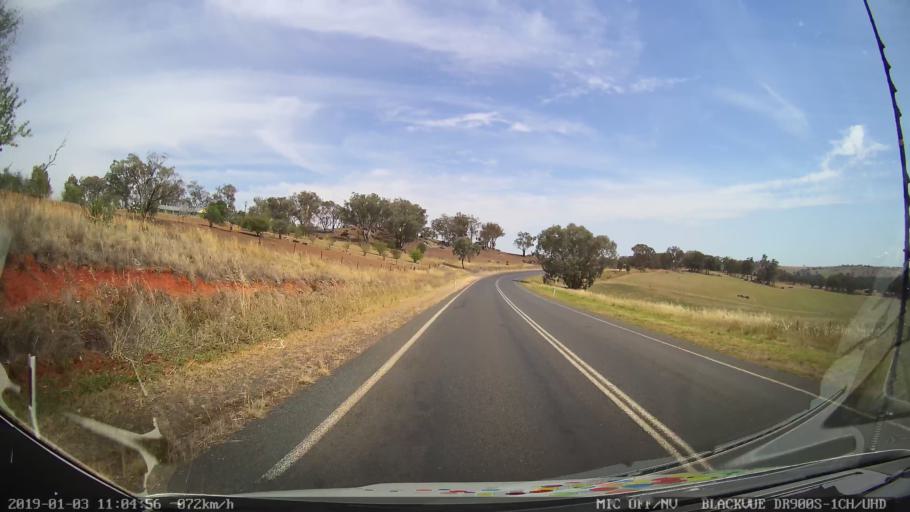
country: AU
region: New South Wales
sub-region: Young
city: Young
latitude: -34.2767
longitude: 148.2872
